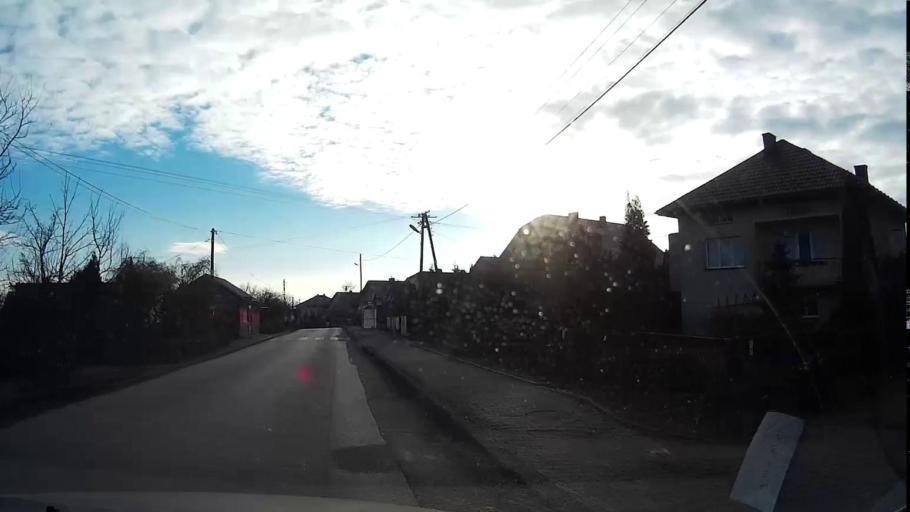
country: PL
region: Lesser Poland Voivodeship
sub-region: Powiat krakowski
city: Sanka
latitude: 50.0593
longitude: 19.6552
